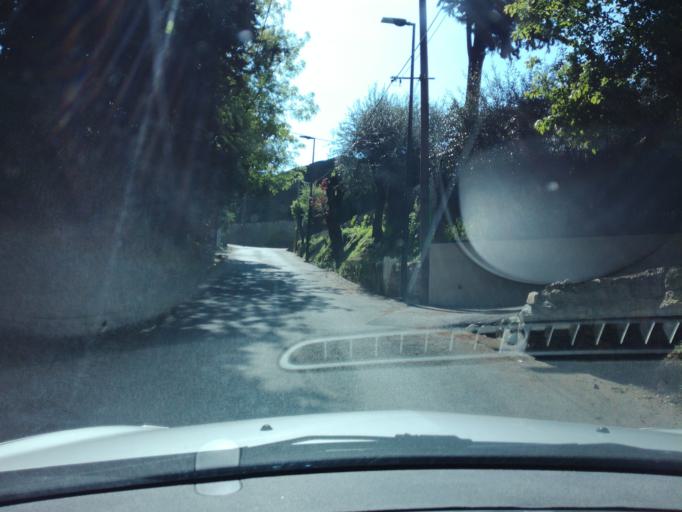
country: FR
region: Provence-Alpes-Cote d'Azur
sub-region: Departement des Alpes-Maritimes
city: Mougins
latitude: 43.6037
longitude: 6.9957
